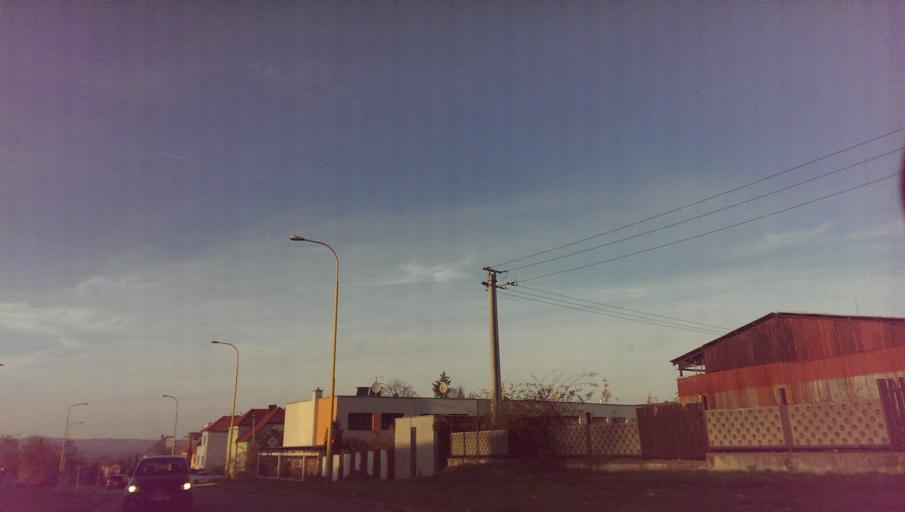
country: CZ
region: Zlin
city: Kunovice
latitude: 49.0597
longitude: 17.4844
